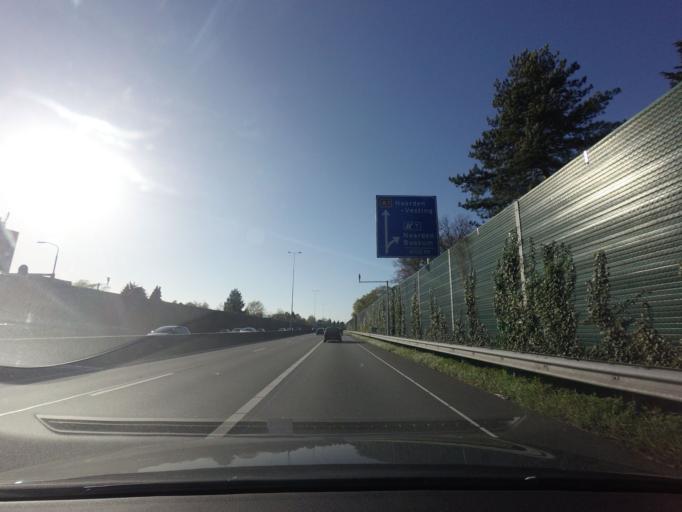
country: NL
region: North Holland
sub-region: Gemeente Bussum
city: Bussum
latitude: 52.2739
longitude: 5.1915
